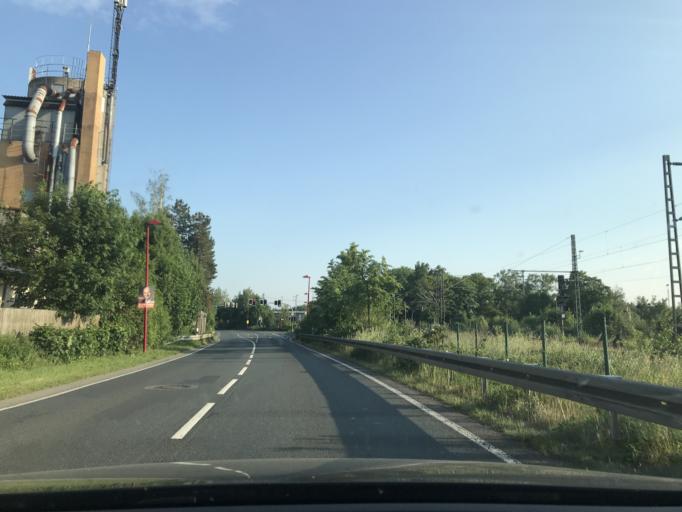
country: DE
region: Lower Saxony
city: Lehrte
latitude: 52.3814
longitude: 9.9723
